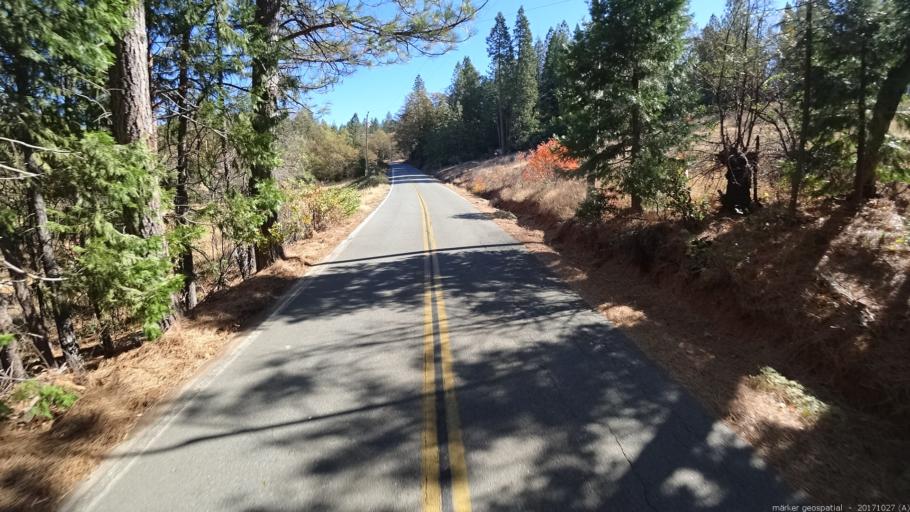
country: US
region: California
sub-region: Shasta County
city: Shingletown
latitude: 40.7555
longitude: -121.9691
